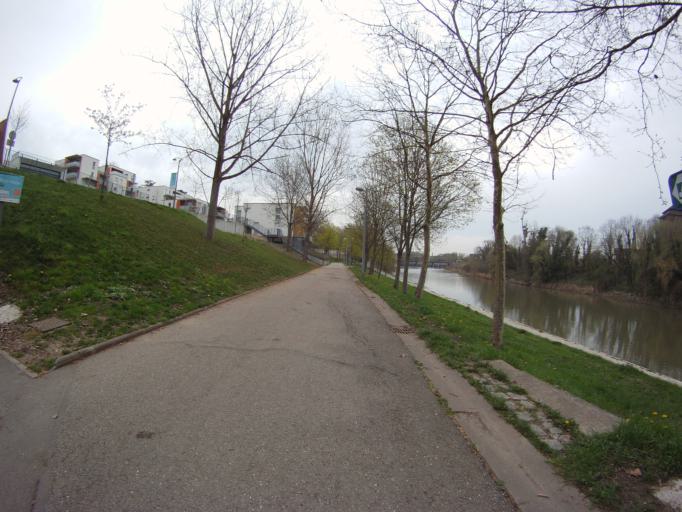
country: FR
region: Lorraine
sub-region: Departement de Meurthe-et-Moselle
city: Malzeville
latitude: 48.7028
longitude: 6.1940
